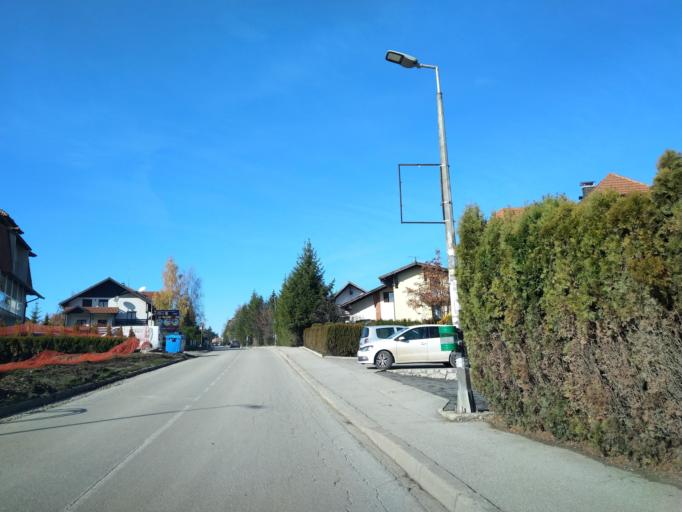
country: RS
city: Zlatibor
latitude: 43.7266
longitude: 19.6913
